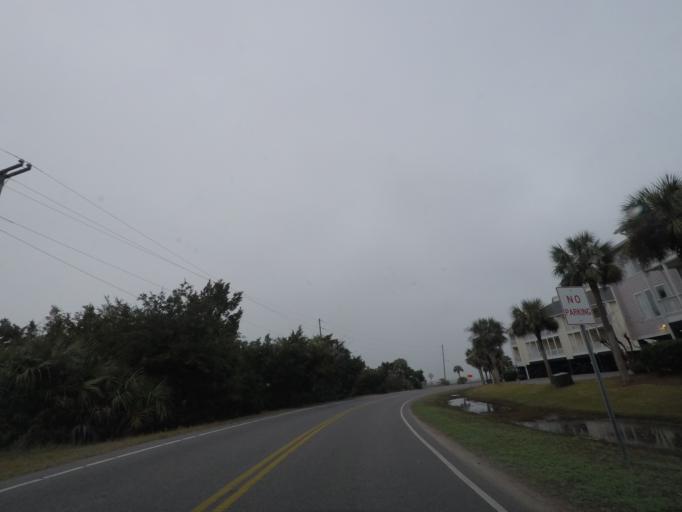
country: US
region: South Carolina
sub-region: Charleston County
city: Seabrook Island
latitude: 32.4917
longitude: -80.3435
